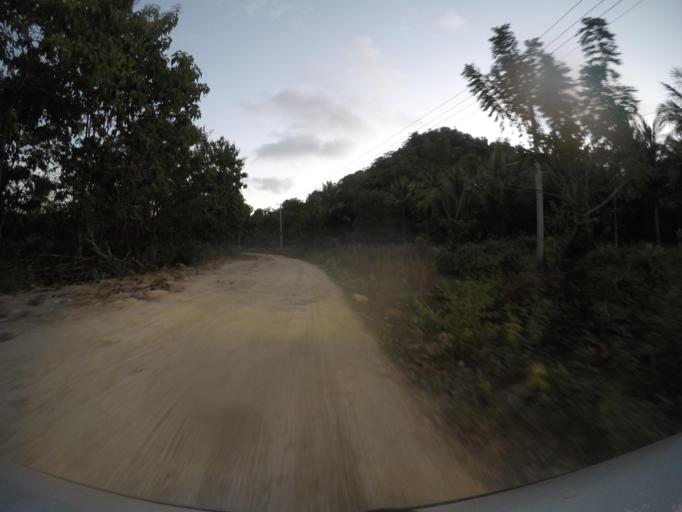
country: TL
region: Viqueque
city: Viqueque
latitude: -8.7921
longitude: 126.6251
